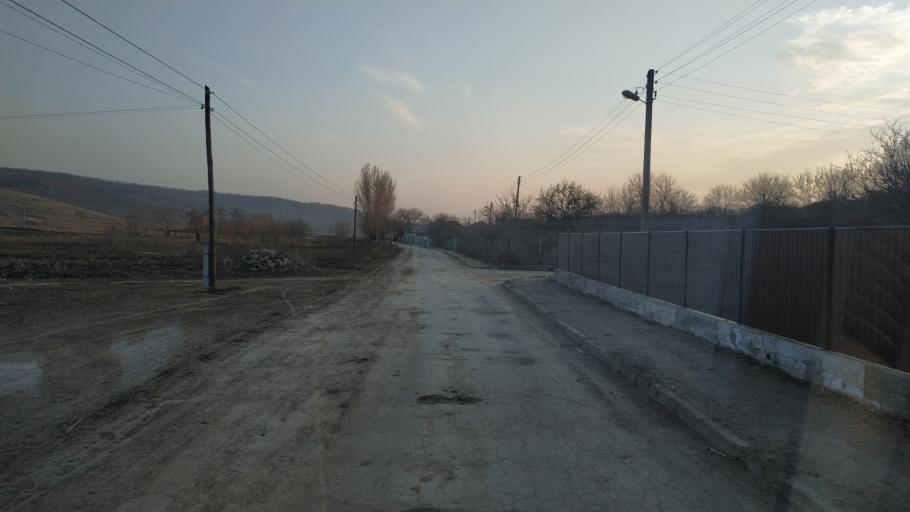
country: MD
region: Hincesti
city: Dancu
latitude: 46.7093
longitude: 28.3453
